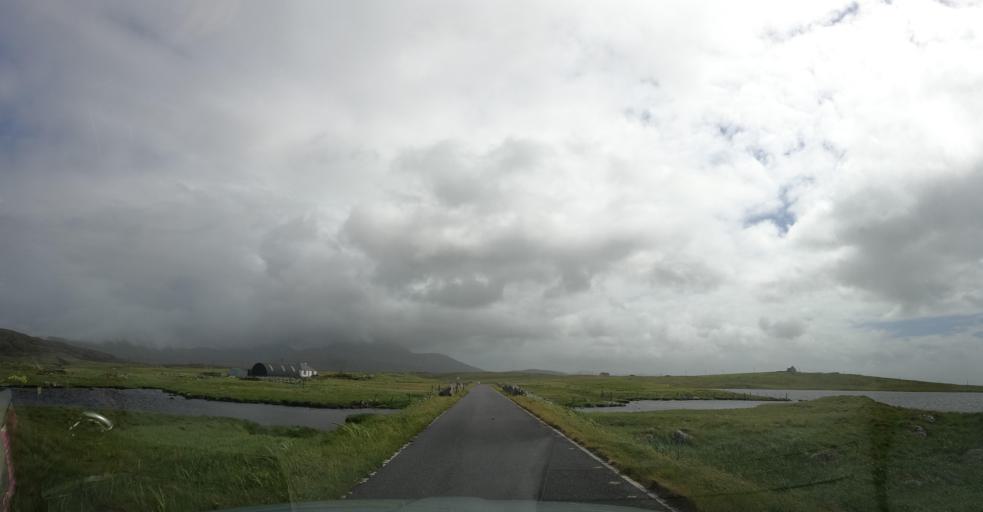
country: GB
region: Scotland
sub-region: Eilean Siar
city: Isle of South Uist
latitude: 57.2949
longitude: -7.3858
